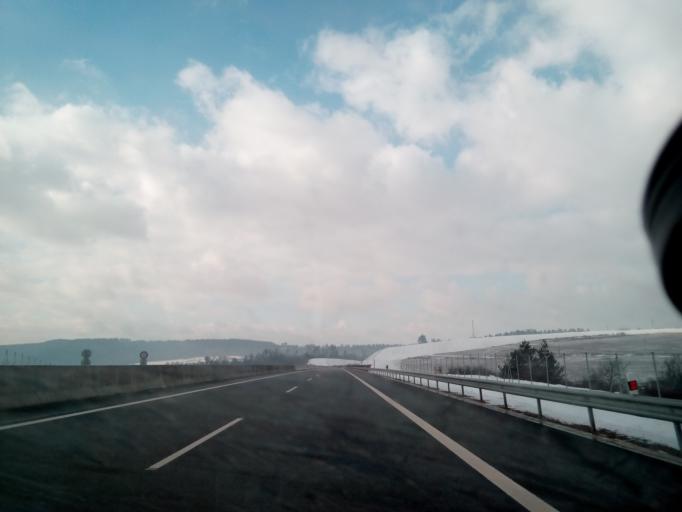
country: SK
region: Presovsky
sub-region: Okres Presov
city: Levoca
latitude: 49.0087
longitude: 20.6592
